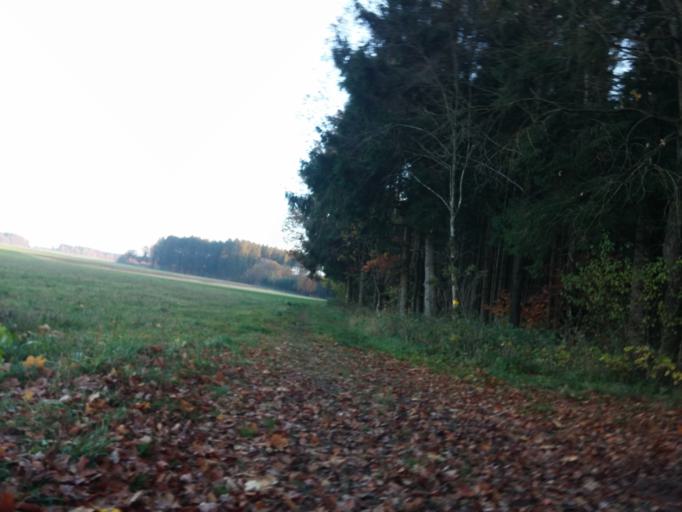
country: DE
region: Bavaria
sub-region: Upper Bavaria
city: Zorneding
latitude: 48.0773
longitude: 11.8529
